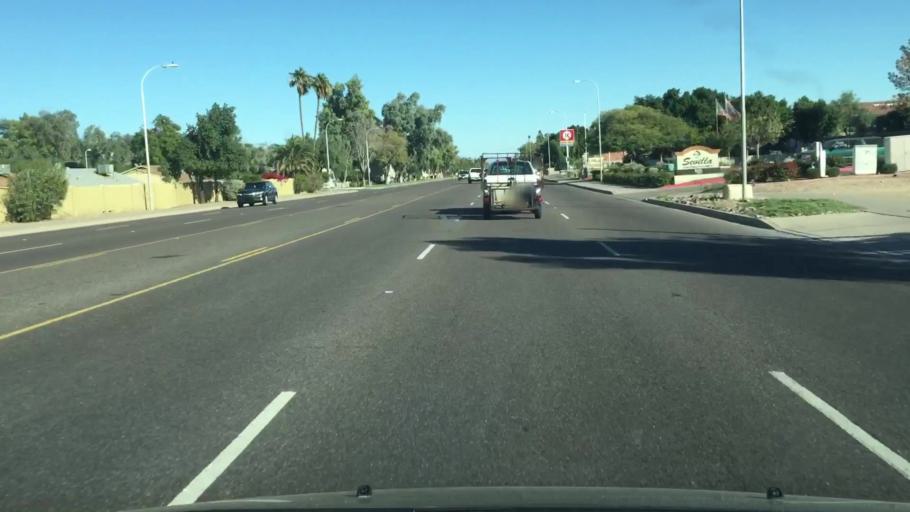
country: US
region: Arizona
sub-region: Maricopa County
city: Guadalupe
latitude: 33.3782
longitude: -111.9568
